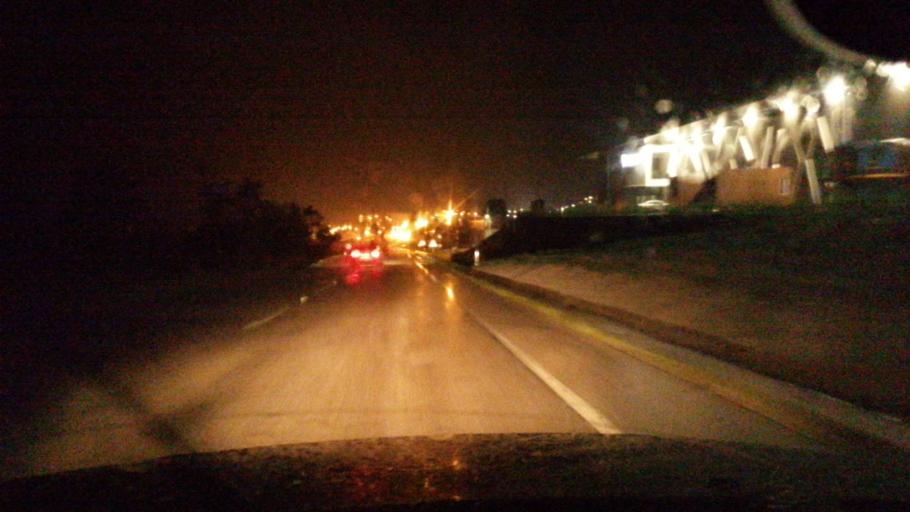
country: PT
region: Viseu
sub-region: Sernancelhe
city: Sernancelhe
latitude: 40.9018
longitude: -7.4772
